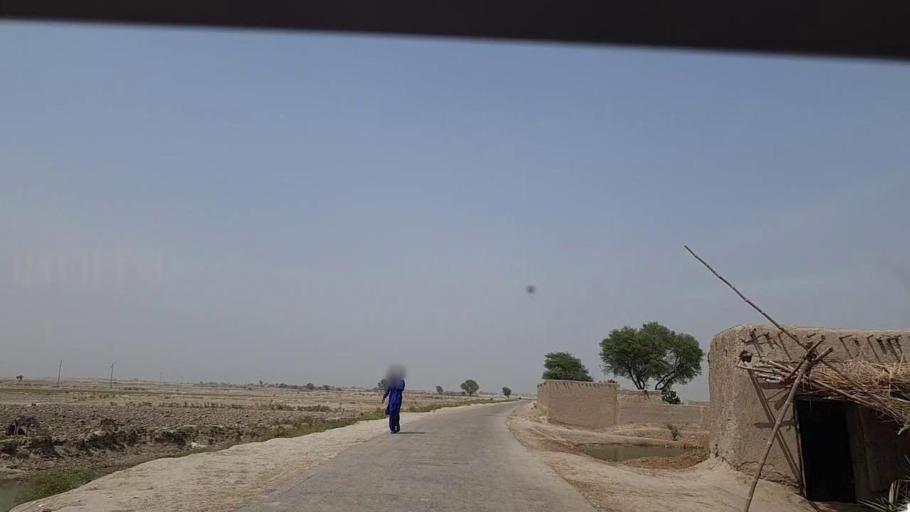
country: PK
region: Sindh
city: Khairpur Nathan Shah
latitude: 27.0538
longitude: 67.6459
